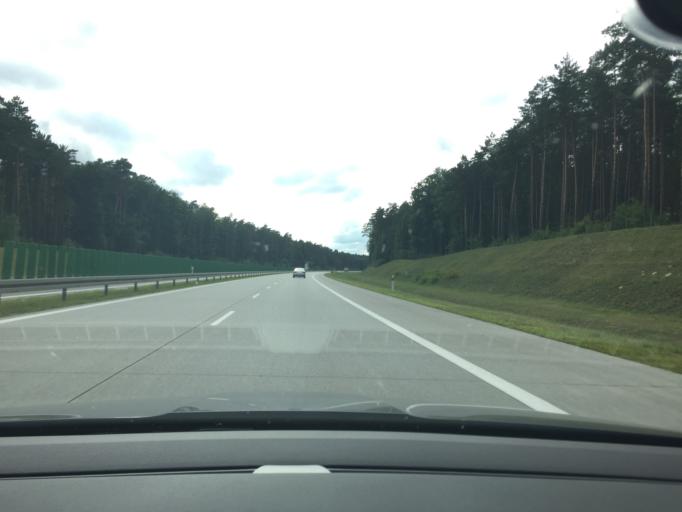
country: PL
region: Lubusz
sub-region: Powiat swiebodzinski
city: Lagow
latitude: 52.3114
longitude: 15.2189
